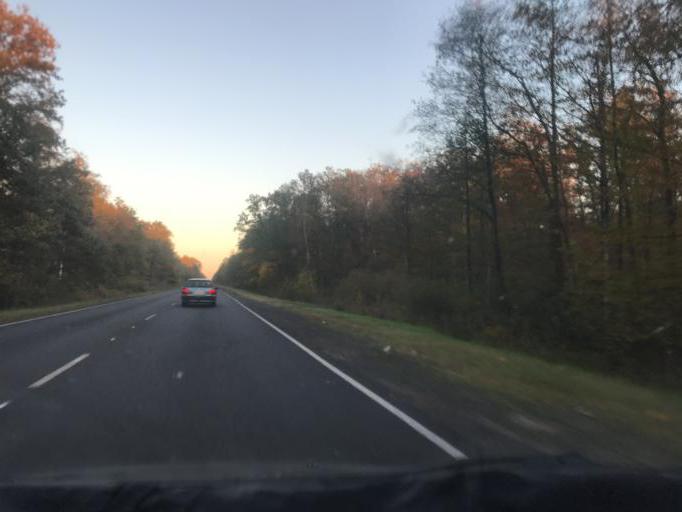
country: BY
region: Gomel
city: Mazyr
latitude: 52.1868
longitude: 29.1403
